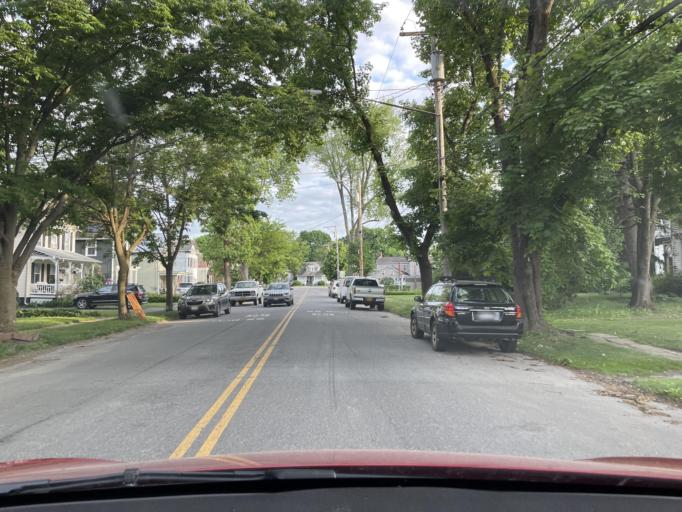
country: US
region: New York
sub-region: Ulster County
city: Saugerties
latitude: 42.0803
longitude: -73.9562
